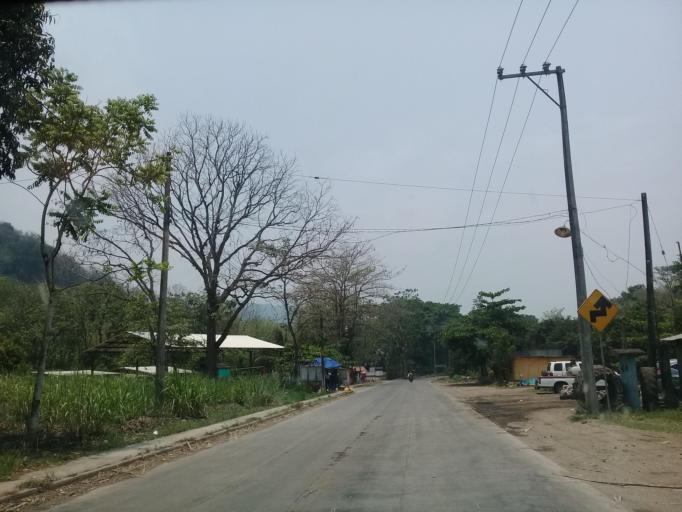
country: MX
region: Veracruz
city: Cosolapa
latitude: 18.5921
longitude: -96.6946
